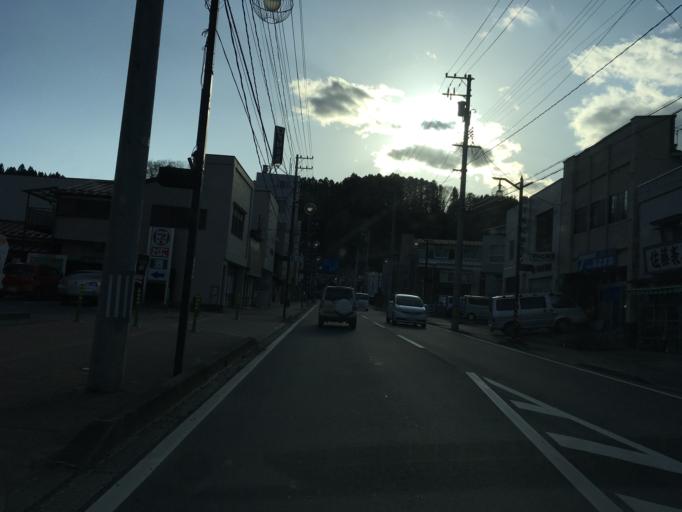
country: JP
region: Iwate
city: Ofunato
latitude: 38.9061
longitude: 141.5663
